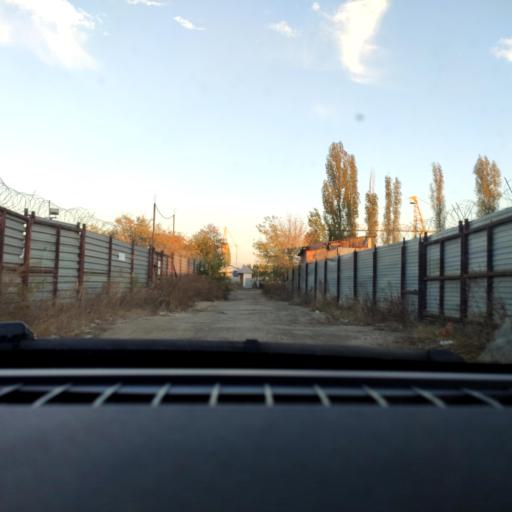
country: RU
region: Voronezj
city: Maslovka
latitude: 51.6408
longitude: 39.2834
